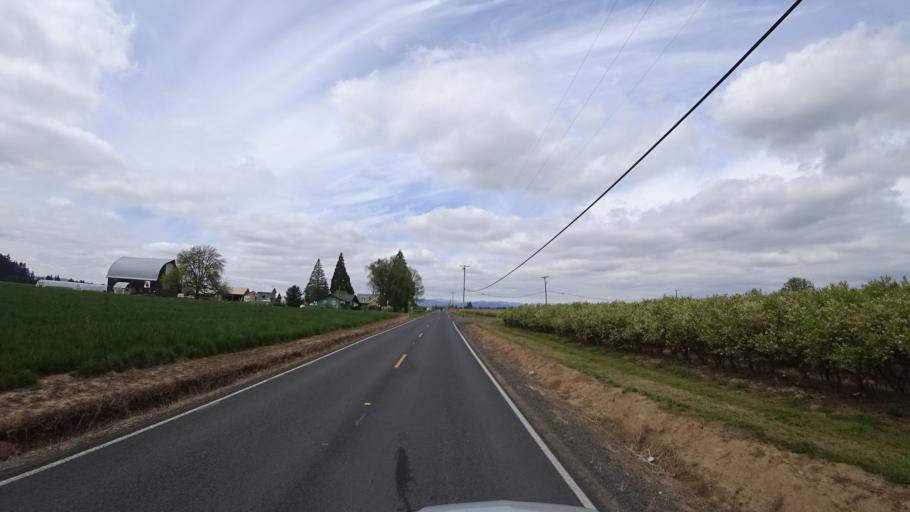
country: US
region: Oregon
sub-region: Washington County
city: Hillsboro
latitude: 45.5439
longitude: -123.0115
